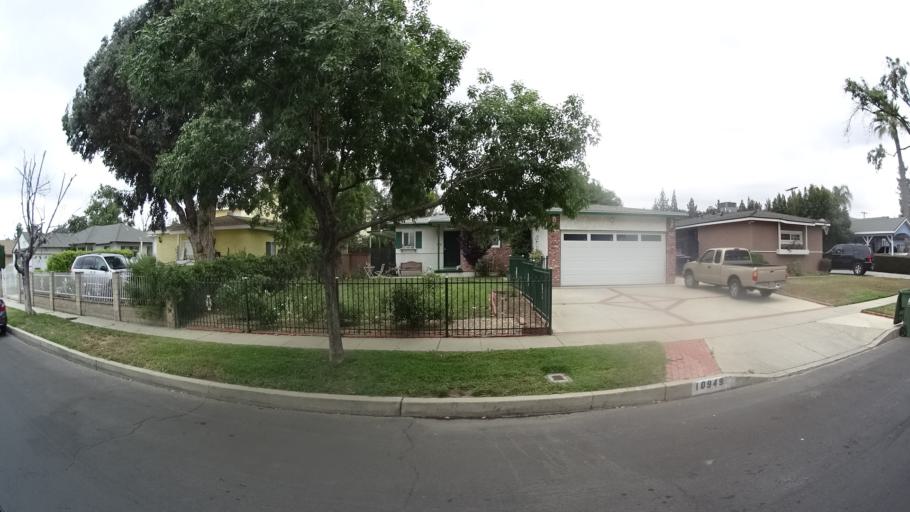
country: US
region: California
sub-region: Los Angeles County
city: San Fernando
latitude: 34.2698
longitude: -118.4707
